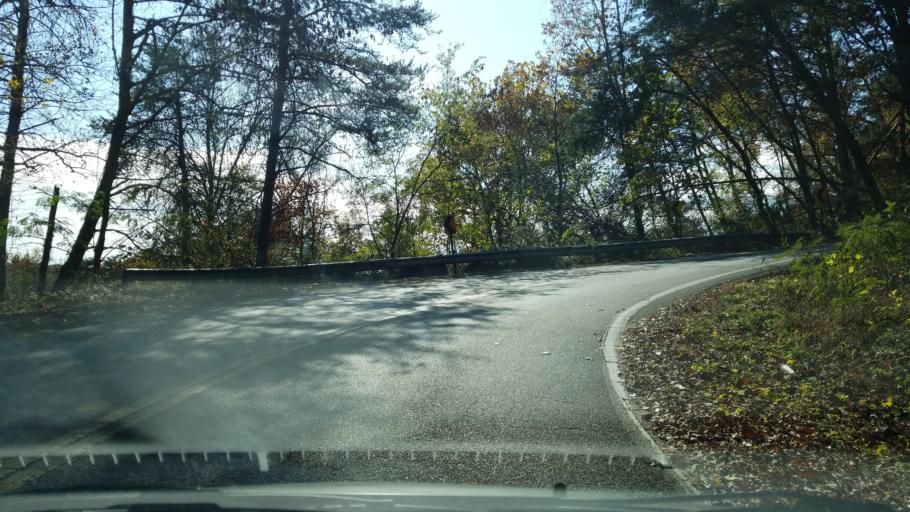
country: US
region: Tennessee
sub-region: Hamilton County
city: Soddy-Daisy
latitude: 35.2430
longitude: -85.1955
